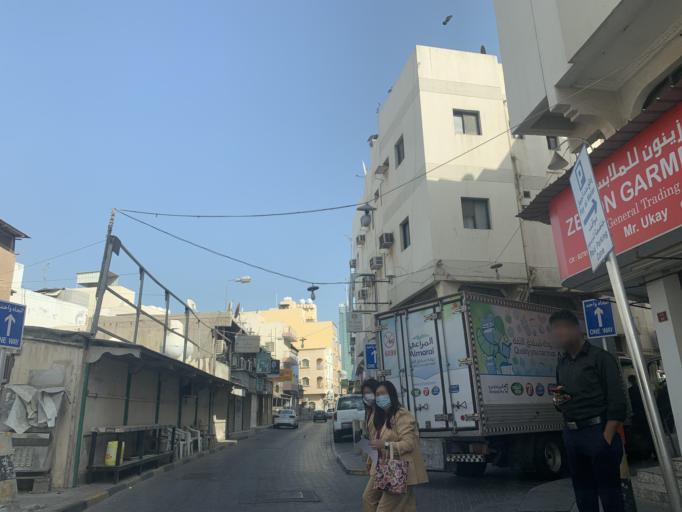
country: BH
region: Manama
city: Manama
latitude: 26.2288
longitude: 50.5783
